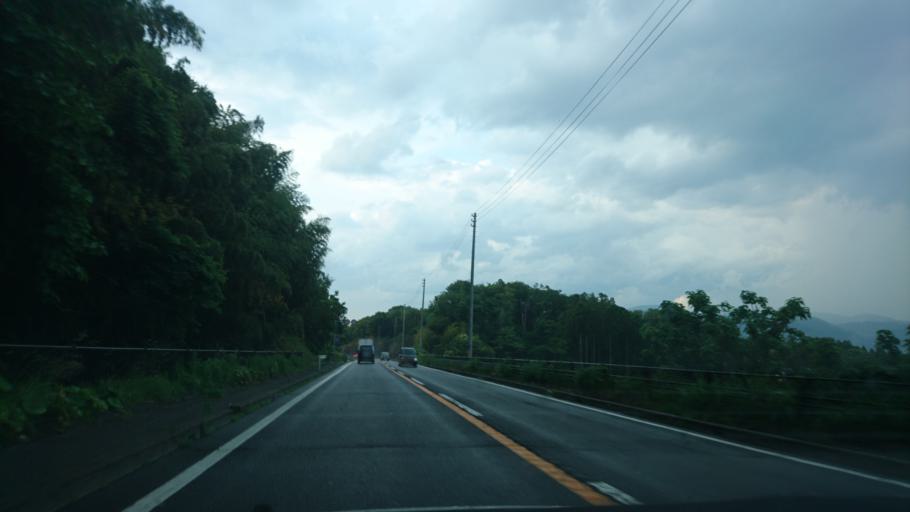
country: JP
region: Iwate
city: Ichinoseki
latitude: 38.9550
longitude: 141.1222
